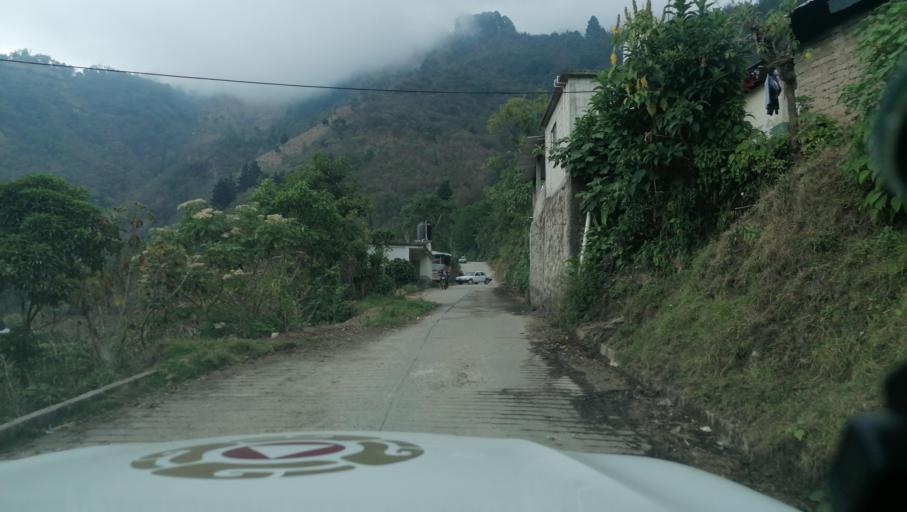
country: GT
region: San Marcos
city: Tacana
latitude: 15.2027
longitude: -92.1810
